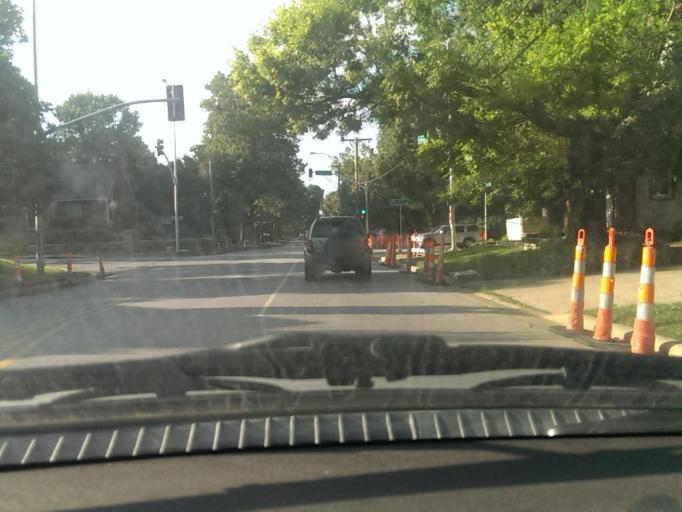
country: US
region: Kansas
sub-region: Johnson County
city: Mission Hills
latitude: 38.9997
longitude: -94.6079
